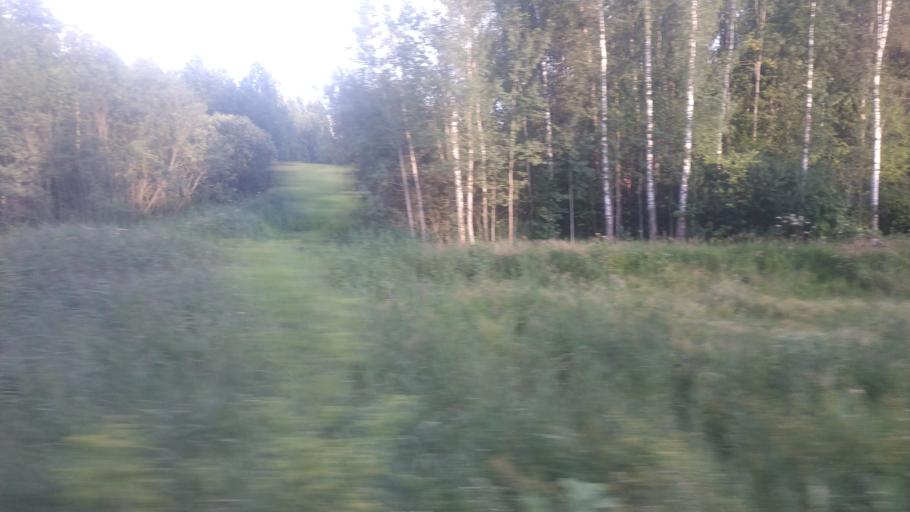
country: RU
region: Moskovskaya
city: Kerva
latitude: 55.5504
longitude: 39.6908
